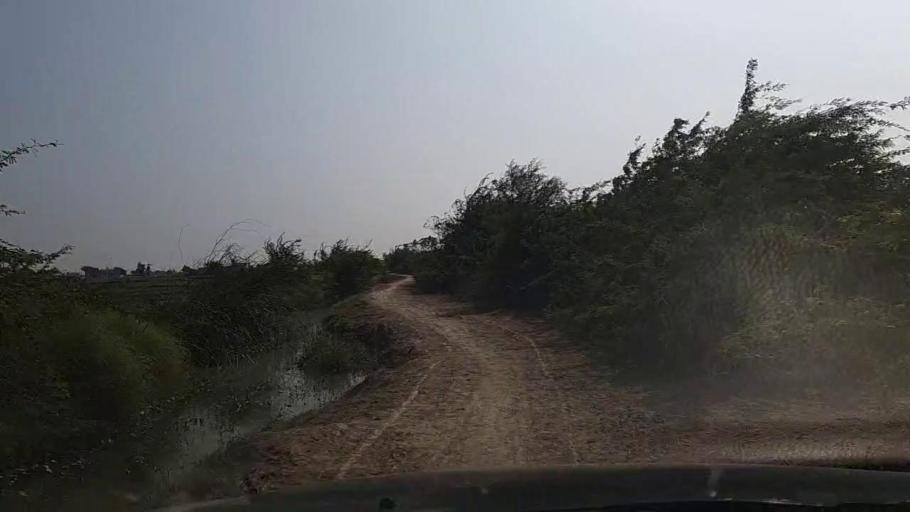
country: PK
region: Sindh
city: Gharo
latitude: 24.7371
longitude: 67.6851
